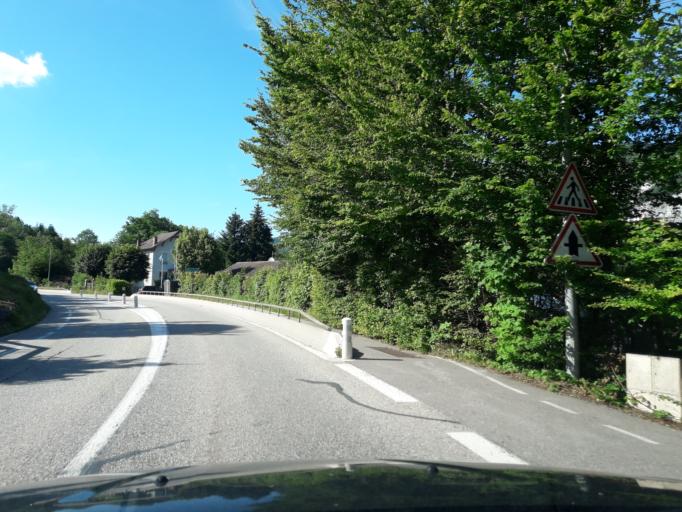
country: FR
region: Rhone-Alpes
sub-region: Departement de la Savoie
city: Novalaise
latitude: 45.5703
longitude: 5.7946
